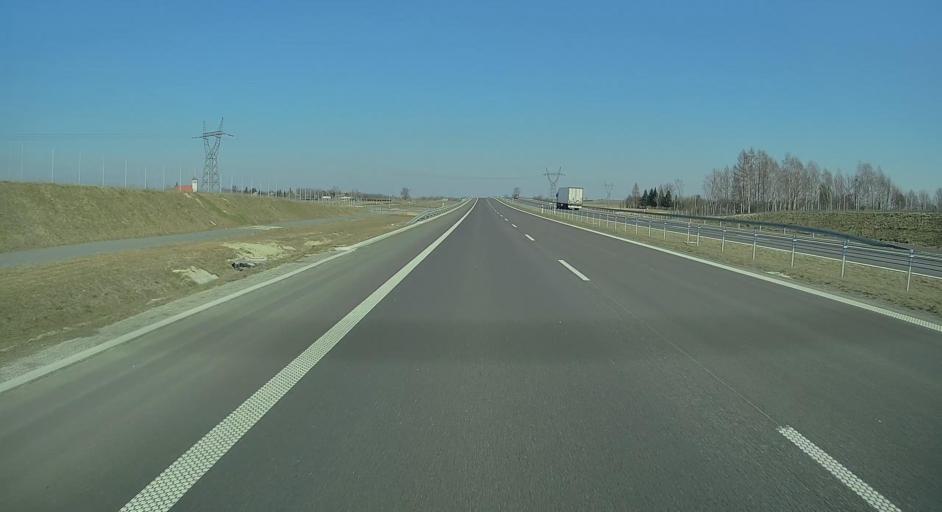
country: PL
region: Lublin Voivodeship
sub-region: Powiat janowski
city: Modliborzyce
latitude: 50.7979
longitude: 22.2950
